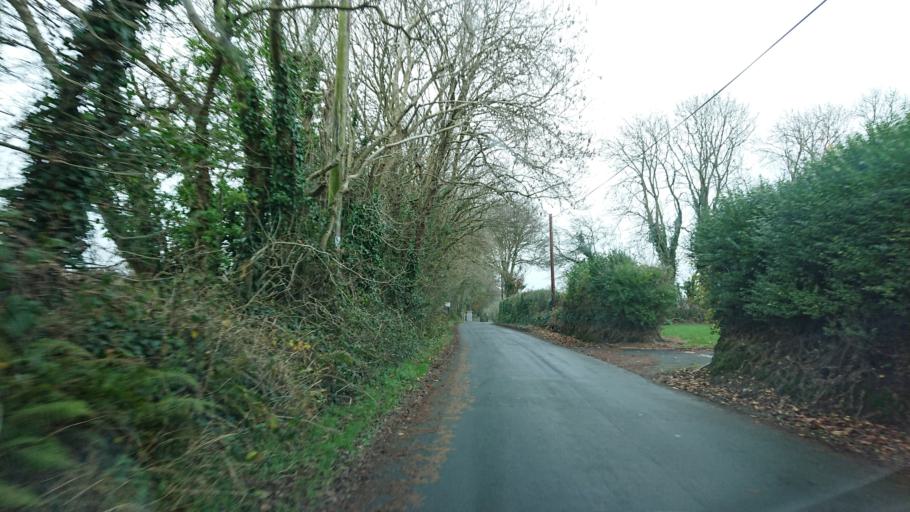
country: IE
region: Munster
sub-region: Waterford
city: Dunmore East
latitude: 52.1954
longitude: -7.0197
